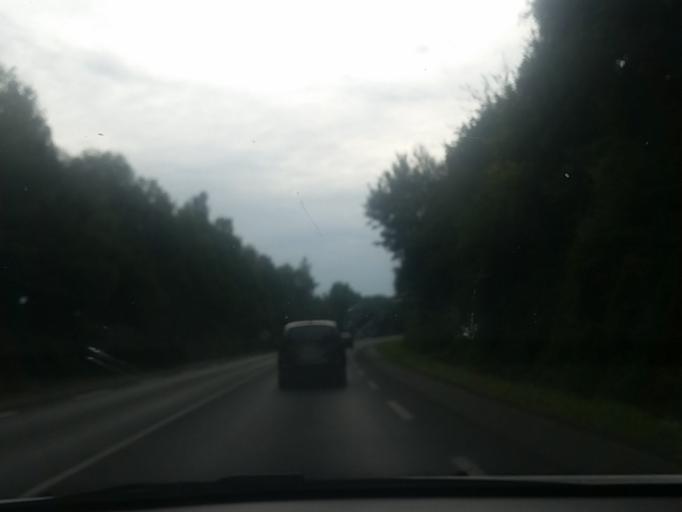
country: FR
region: Pays de la Loire
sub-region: Departement de la Vendee
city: Saint-Fulgent
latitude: 46.8628
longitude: -1.1774
